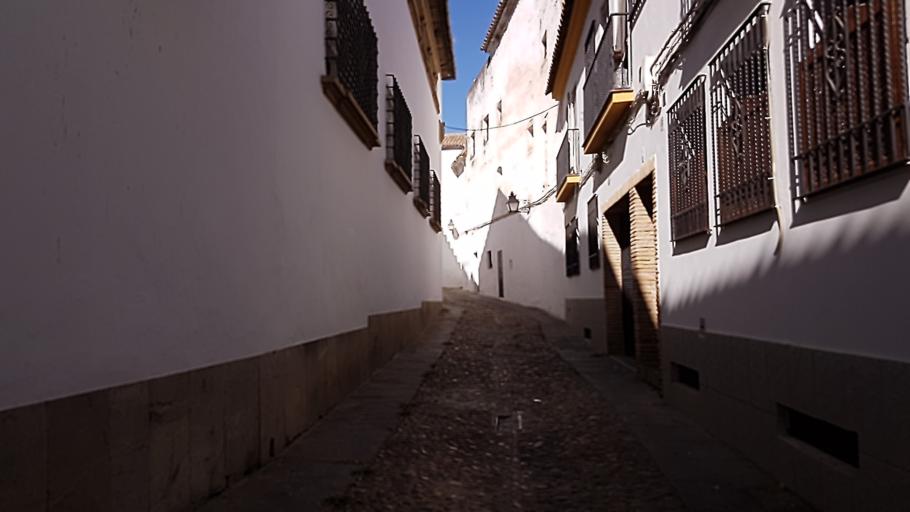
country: ES
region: Andalusia
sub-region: Province of Cordoba
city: Cordoba
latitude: 37.8818
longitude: -4.7776
